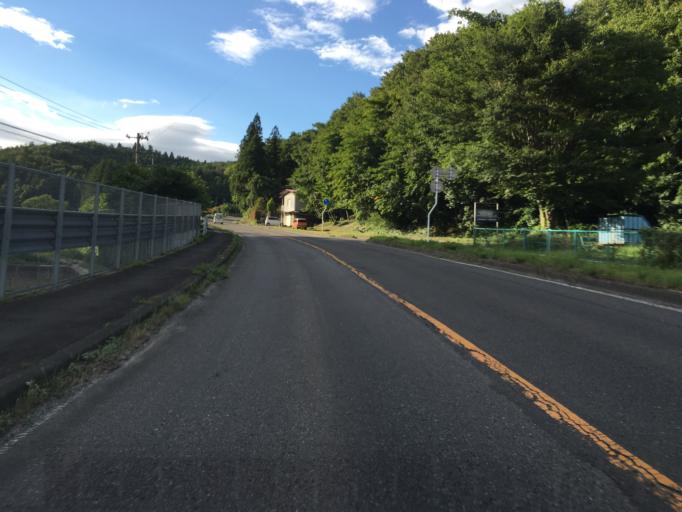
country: JP
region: Fukushima
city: Nihommatsu
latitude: 37.6379
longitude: 140.4645
